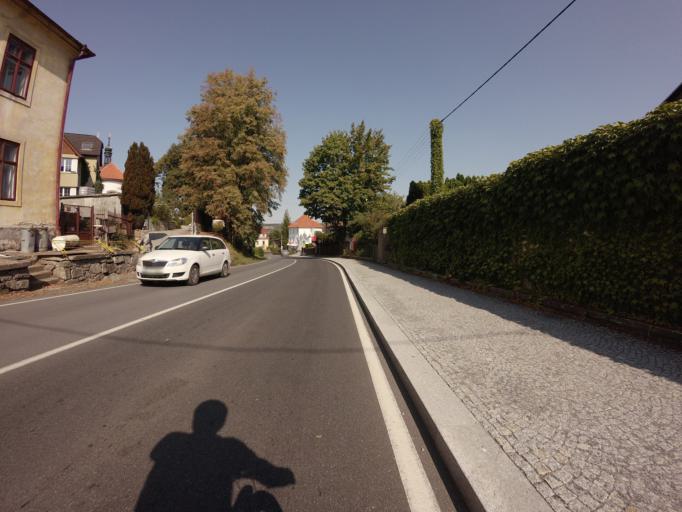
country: CZ
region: Central Bohemia
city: Tynec nad Sazavou
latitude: 49.8293
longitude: 14.5939
